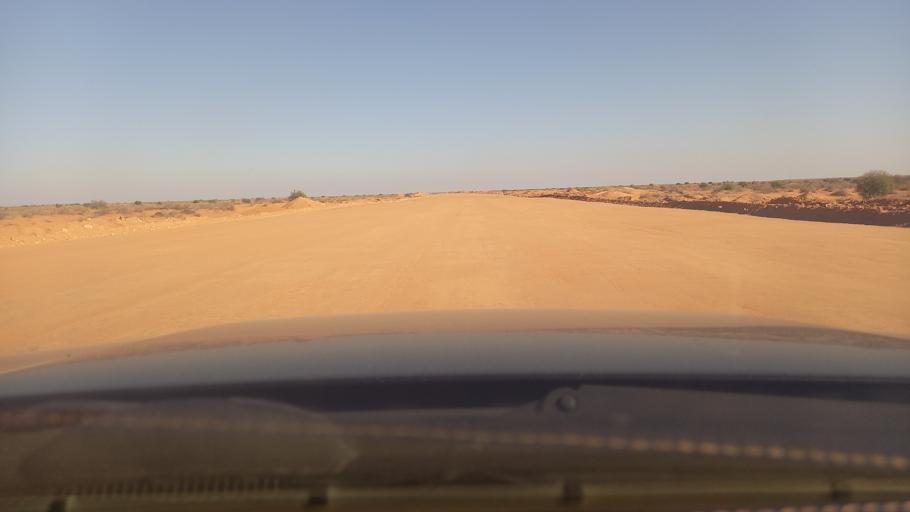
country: TN
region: Madanin
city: Medenine
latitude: 33.1569
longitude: 10.5150
